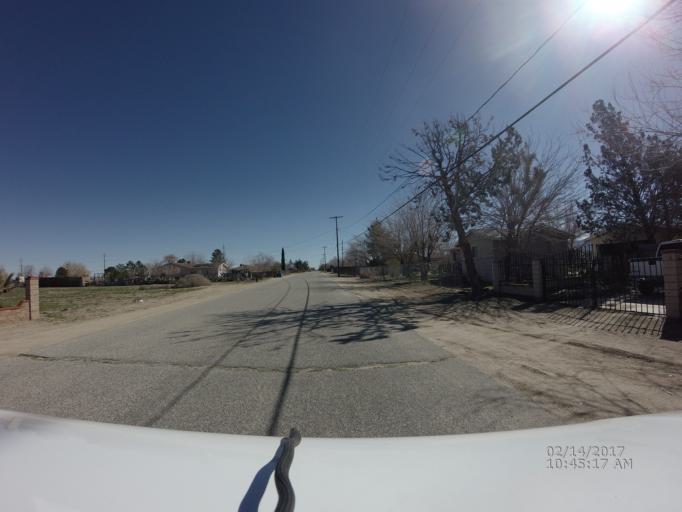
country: US
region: California
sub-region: Los Angeles County
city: Littlerock
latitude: 34.5671
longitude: -117.9356
